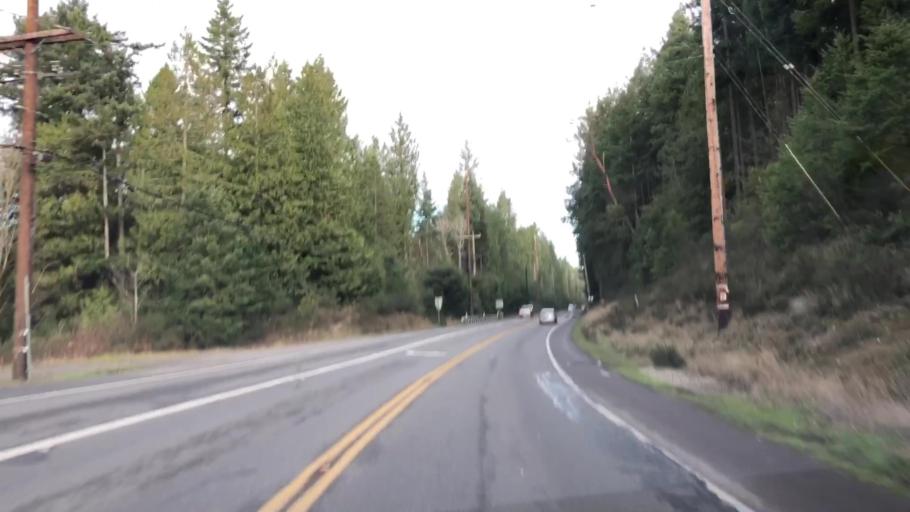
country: US
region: Washington
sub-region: Kitsap County
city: Suquamish
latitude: 47.7148
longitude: -122.5710
